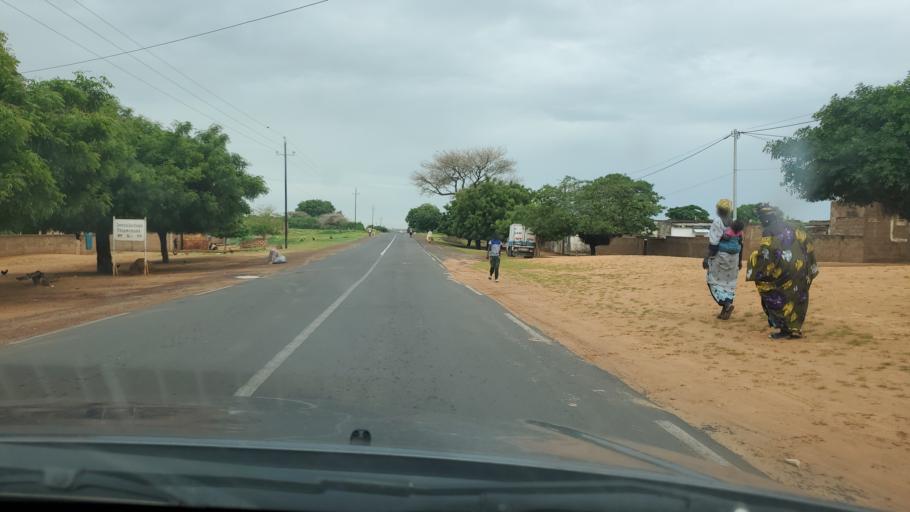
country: SN
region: Thies
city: Mekhe
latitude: 15.1338
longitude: -16.8566
